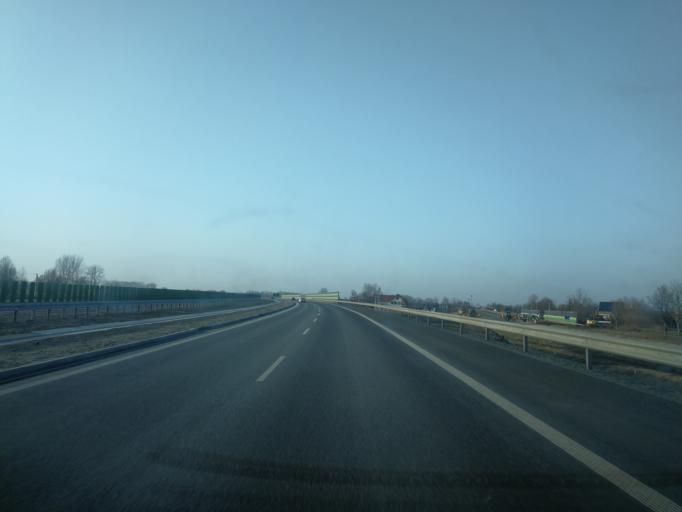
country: PL
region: Warmian-Masurian Voivodeship
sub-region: Powiat elblaski
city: Elblag
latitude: 54.1576
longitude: 19.3623
